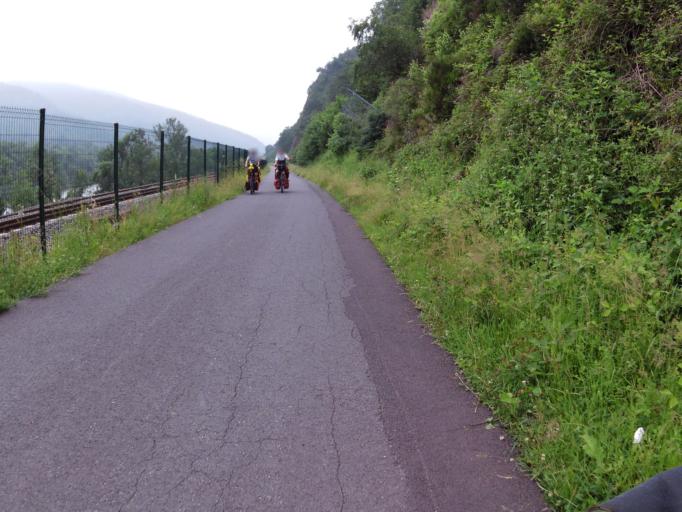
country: FR
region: Champagne-Ardenne
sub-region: Departement des Ardennes
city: Revin
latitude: 49.9486
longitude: 4.6540
